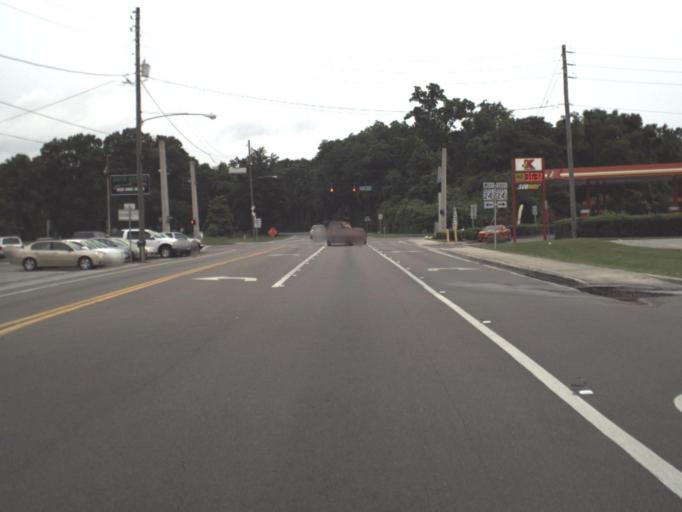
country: US
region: Florida
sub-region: Alachua County
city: Archer
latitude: 29.5361
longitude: -82.5191
